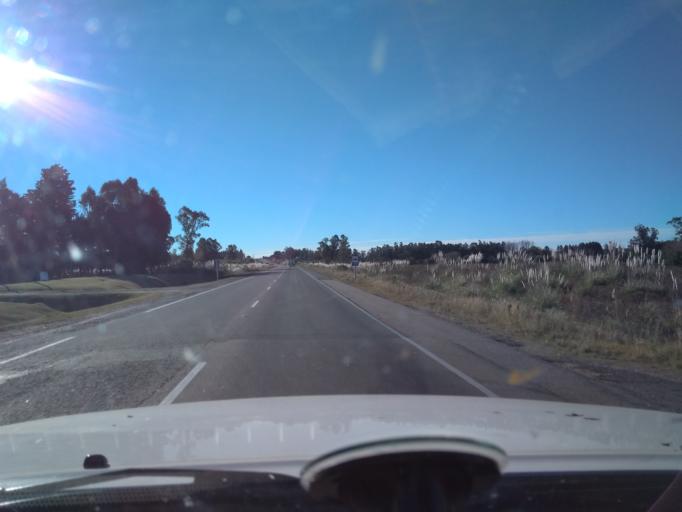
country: UY
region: Canelones
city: Sauce
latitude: -34.5980
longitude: -56.0507
